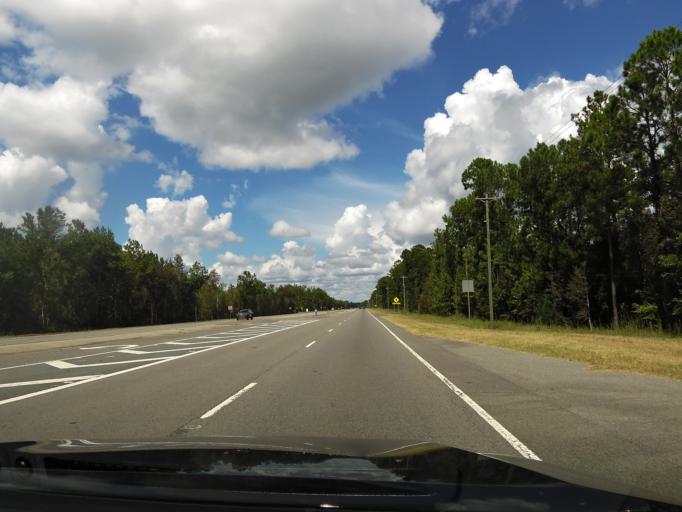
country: US
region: Georgia
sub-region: Charlton County
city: Folkston
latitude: 30.7843
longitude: -81.9799
